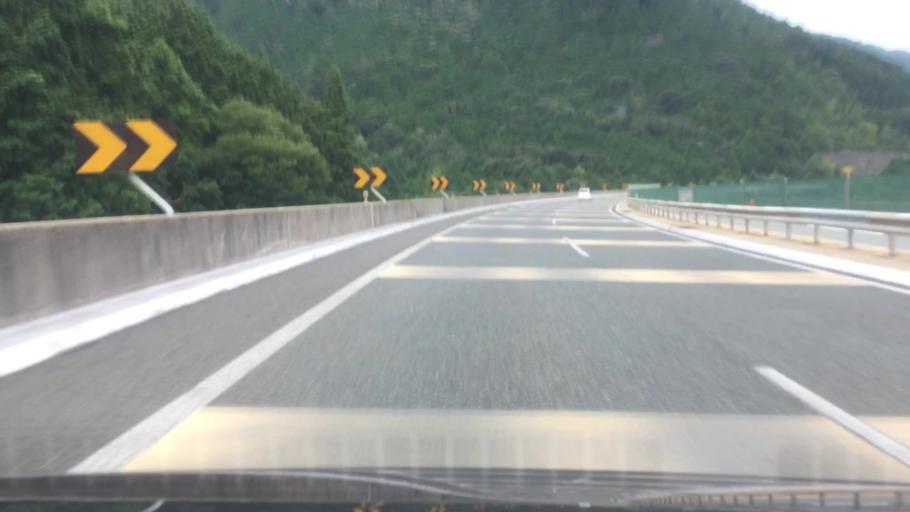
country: JP
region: Hyogo
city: Sasayama
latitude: 35.1382
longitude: 135.1427
